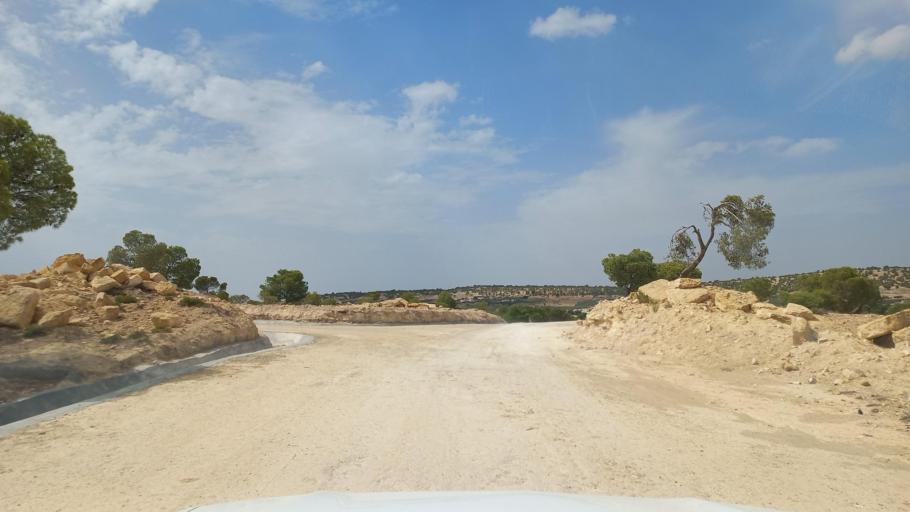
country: TN
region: Al Qasrayn
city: Kasserine
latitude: 35.3842
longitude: 8.8678
